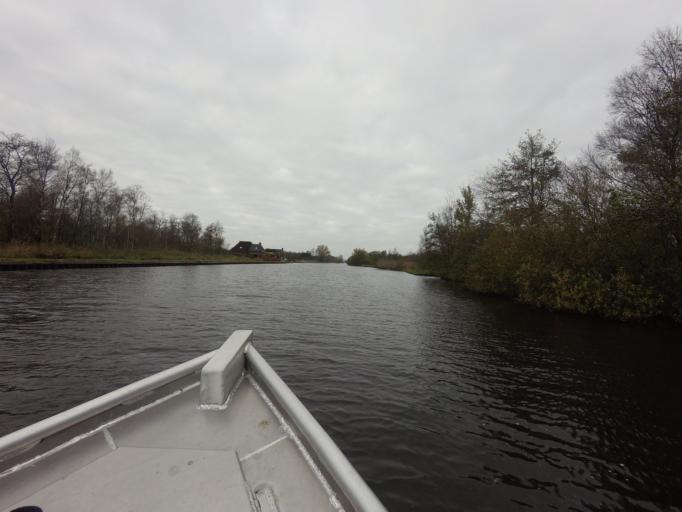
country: NL
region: Overijssel
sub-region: Gemeente Steenwijkerland
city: Oldemarkt
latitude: 52.7922
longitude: 5.9355
